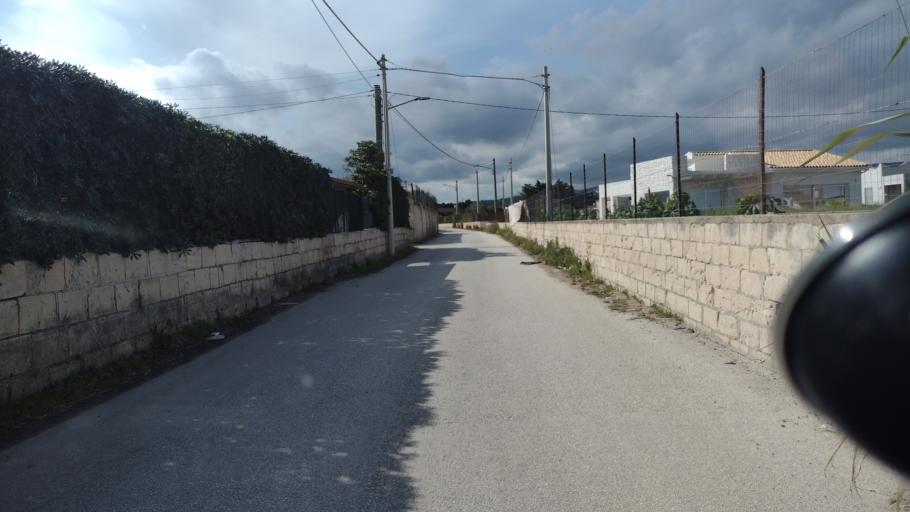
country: IT
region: Sicily
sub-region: Provincia di Siracusa
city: Avola
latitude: 36.8858
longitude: 15.1381
